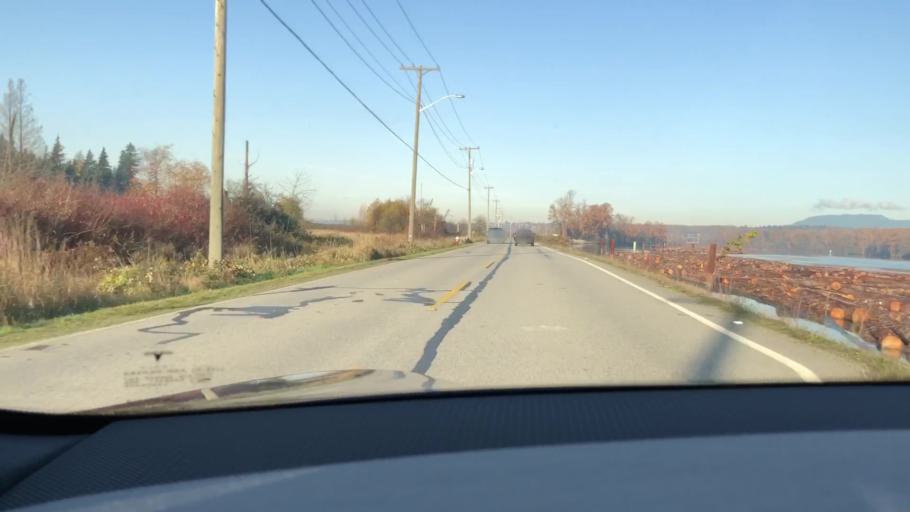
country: CA
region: British Columbia
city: New Westminster
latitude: 49.1834
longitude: -122.9910
